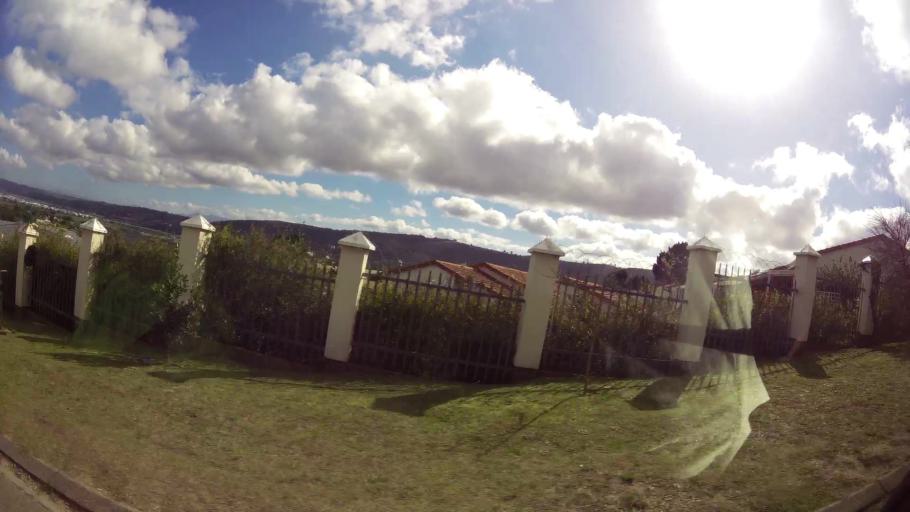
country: ZA
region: Western Cape
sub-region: Eden District Municipality
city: Knysna
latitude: -34.0520
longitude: 23.0796
